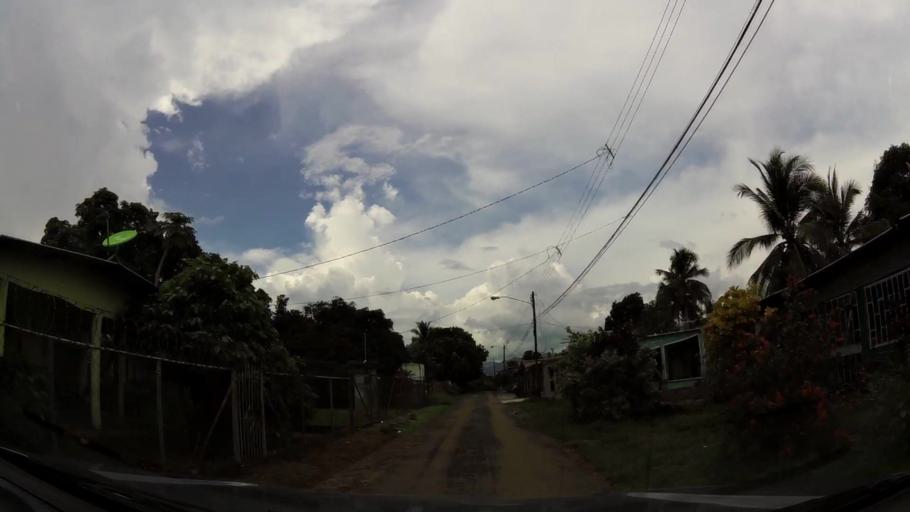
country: PA
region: Panama
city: Cabra Numero Uno
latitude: 9.1082
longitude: -79.3252
